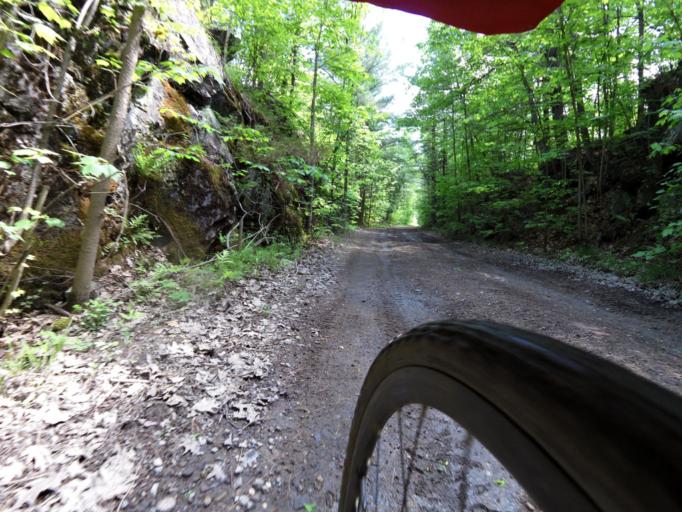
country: CA
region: Ontario
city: Renfrew
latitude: 45.2183
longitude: -76.6929
